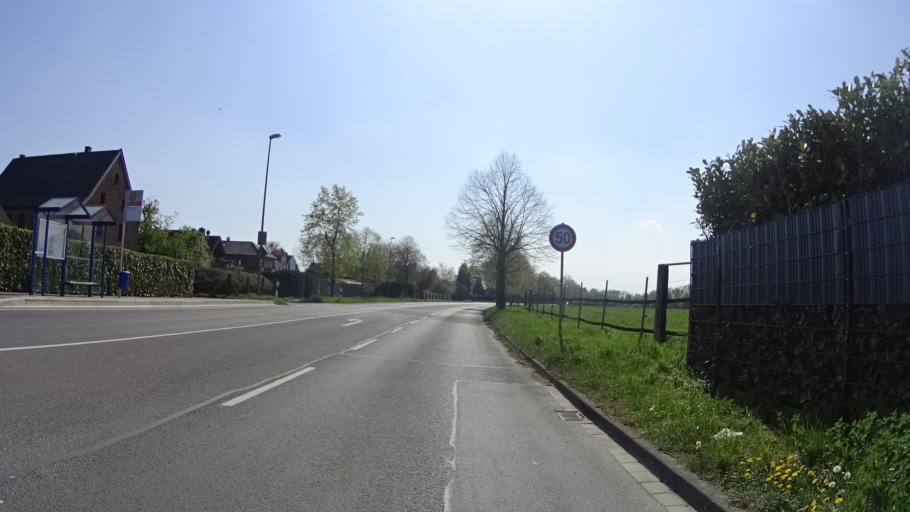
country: DE
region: North Rhine-Westphalia
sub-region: Regierungsbezirk Dusseldorf
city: Meerbusch
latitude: 51.2967
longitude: 6.7148
